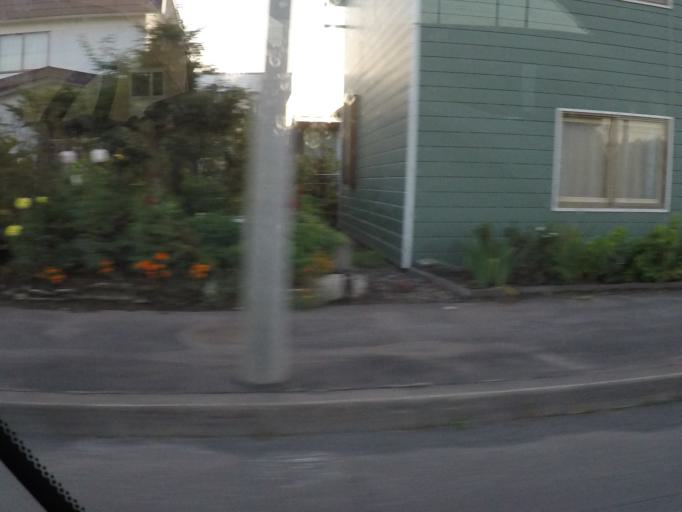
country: JP
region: Hokkaido
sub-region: Asahikawa-shi
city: Asahikawa
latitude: 43.6408
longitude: 142.4525
